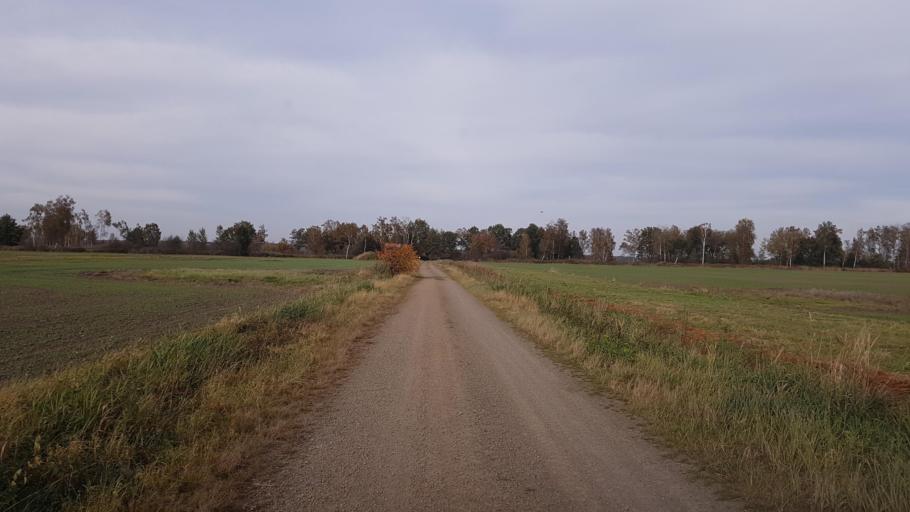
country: DE
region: Brandenburg
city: Schraden
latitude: 51.4564
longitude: 13.6910
